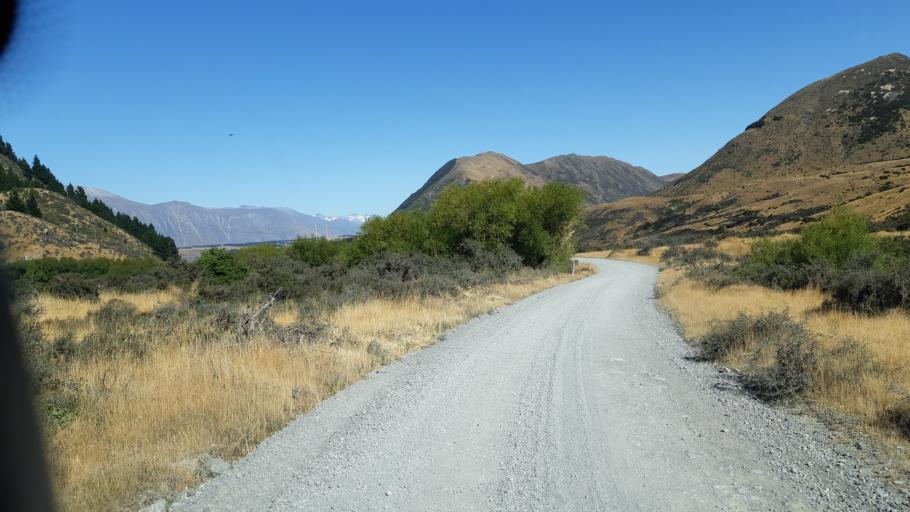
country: NZ
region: Canterbury
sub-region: Ashburton District
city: Methven
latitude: -43.3417
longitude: 171.6115
